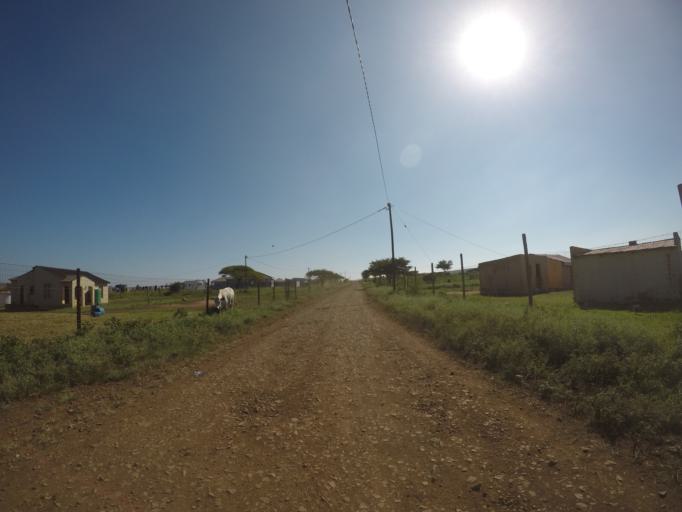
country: ZA
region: KwaZulu-Natal
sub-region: uThungulu District Municipality
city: Empangeni
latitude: -28.5706
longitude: 31.7348
